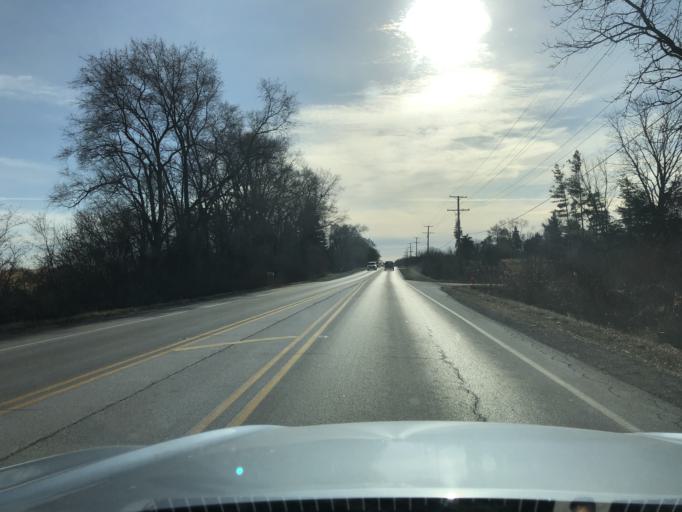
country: US
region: Illinois
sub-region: Lake County
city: Grandwood Park
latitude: 42.3913
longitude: -88.0042
